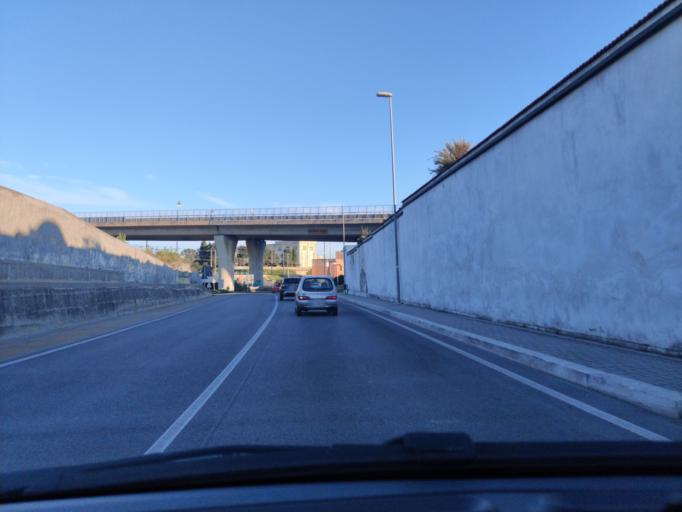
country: IT
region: Latium
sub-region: Citta metropolitana di Roma Capitale
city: Civitavecchia
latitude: 42.1046
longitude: 11.7850
